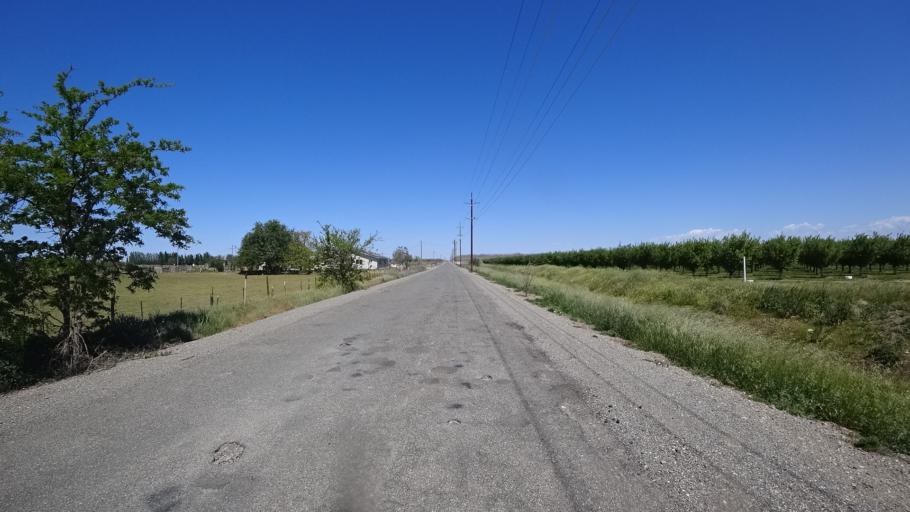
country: US
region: California
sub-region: Glenn County
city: Orland
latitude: 39.7733
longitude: -122.1409
